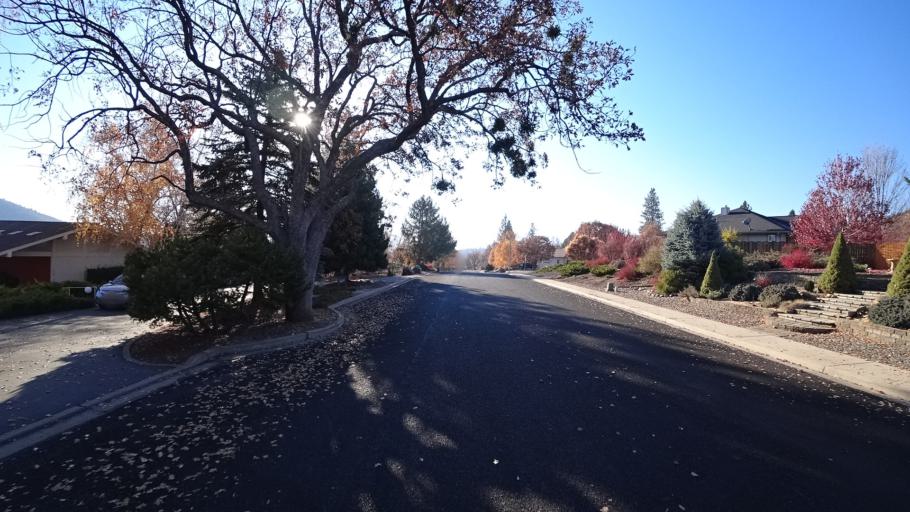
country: US
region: California
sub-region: Siskiyou County
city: Yreka
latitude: 41.7254
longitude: -122.6507
